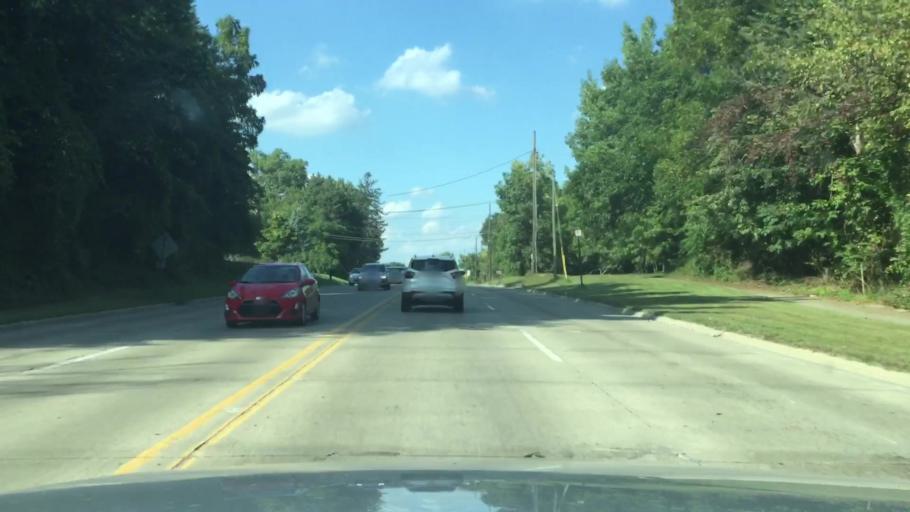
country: US
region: Michigan
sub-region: Wayne County
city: Westland
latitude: 42.3379
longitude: -83.4093
